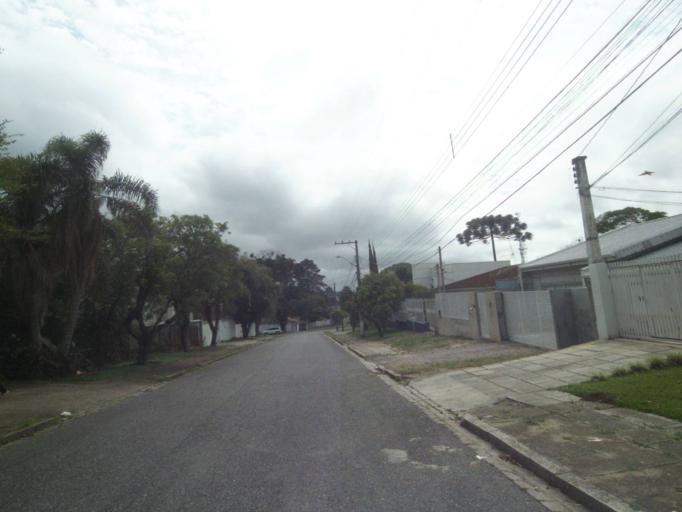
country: BR
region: Parana
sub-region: Curitiba
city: Curitiba
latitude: -25.4267
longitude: -49.2407
